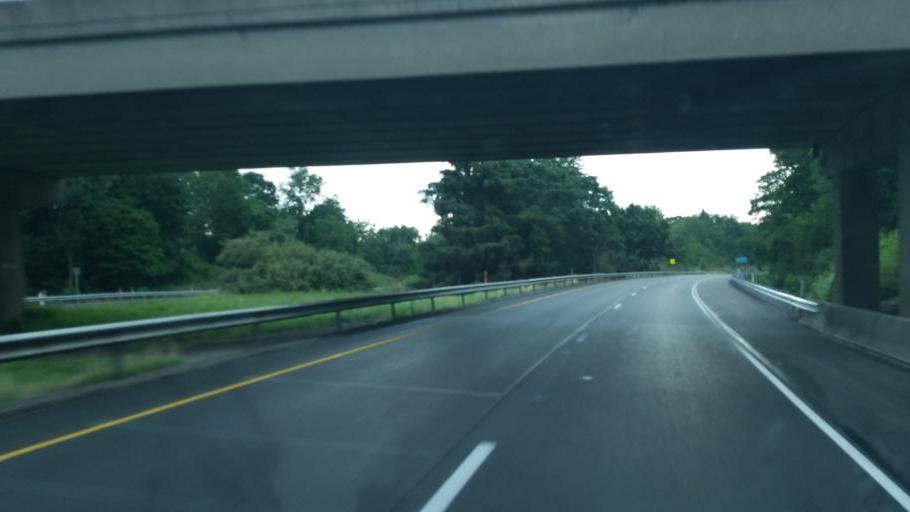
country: US
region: Pennsylvania
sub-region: Butler County
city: Zelienople
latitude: 40.7853
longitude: -80.1238
